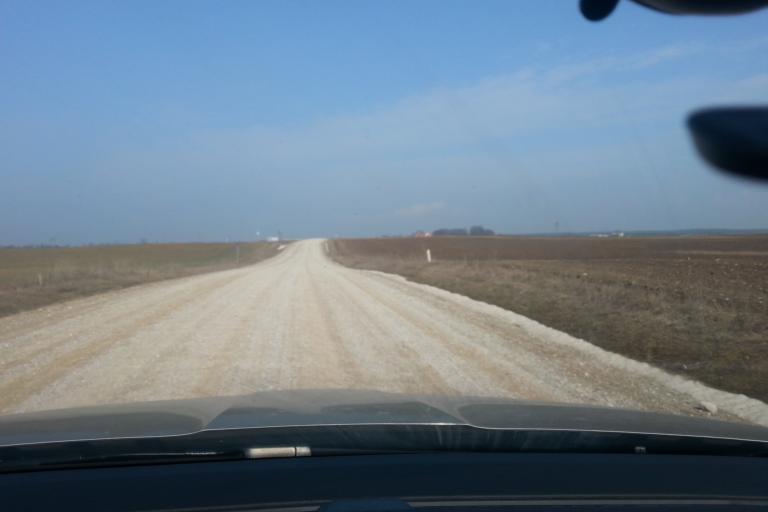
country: LT
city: Trakai
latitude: 54.5959
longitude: 24.9778
